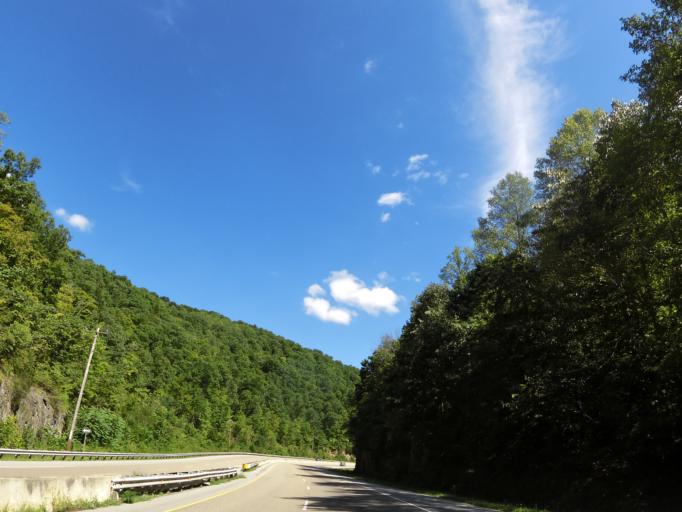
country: US
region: Tennessee
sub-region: Grainger County
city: Rutledge
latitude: 36.3674
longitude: -83.4365
